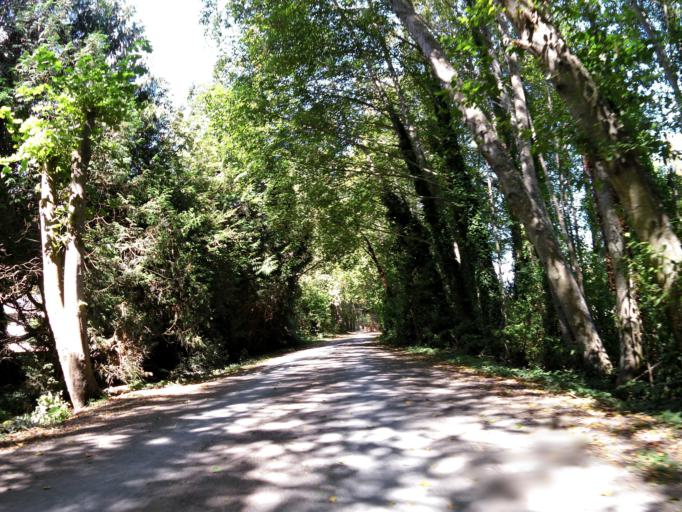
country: CA
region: British Columbia
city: Victoria
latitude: 48.5357
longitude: -123.3781
